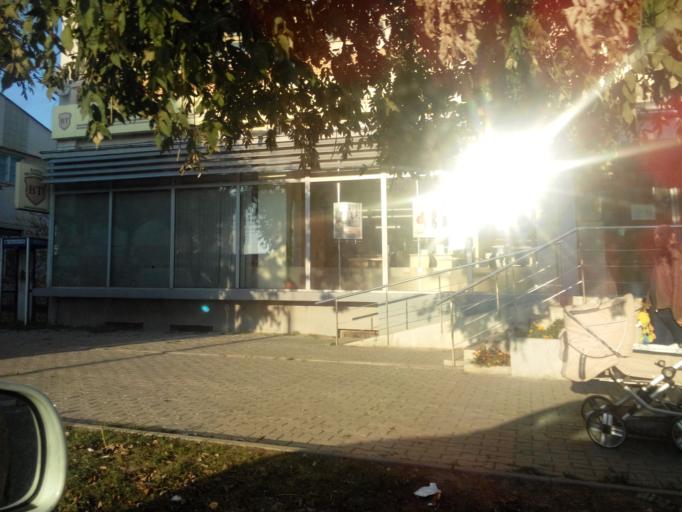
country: RO
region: Vrancea
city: Adjud
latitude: 46.1001
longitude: 27.1808
